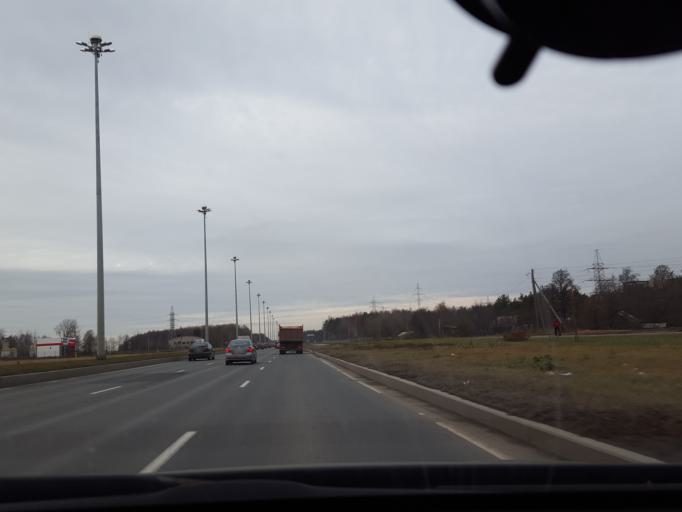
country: RU
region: Leningrad
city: Untolovo
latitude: 60.0420
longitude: 30.2397
